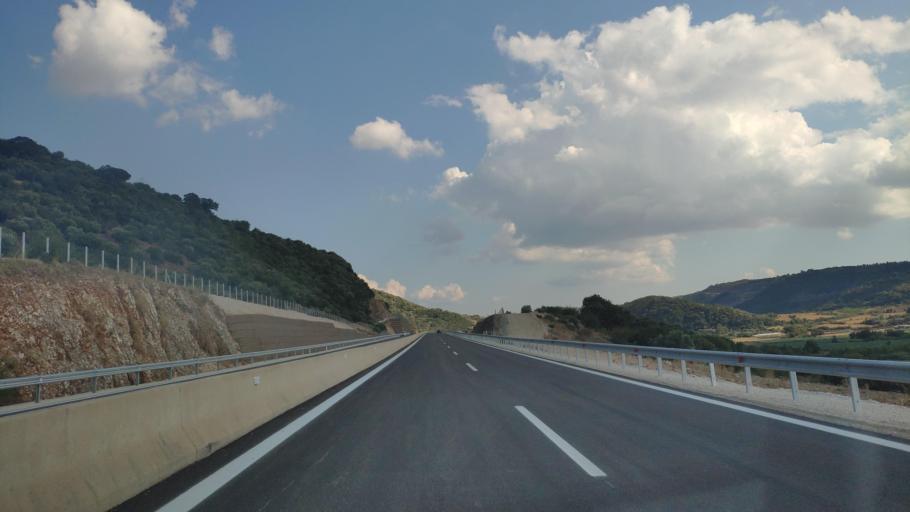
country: GR
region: West Greece
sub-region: Nomos Aitolias kai Akarnanias
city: Katouna
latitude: 38.8000
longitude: 21.1347
